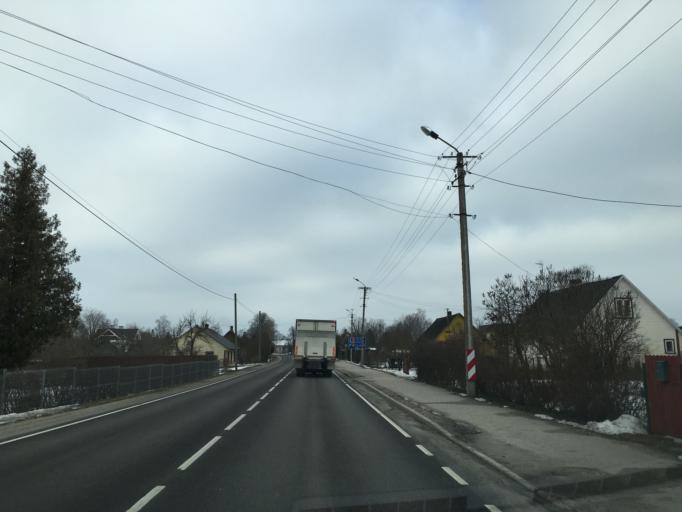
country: EE
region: Tartu
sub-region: Elva linn
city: Elva
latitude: 58.1454
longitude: 26.2526
